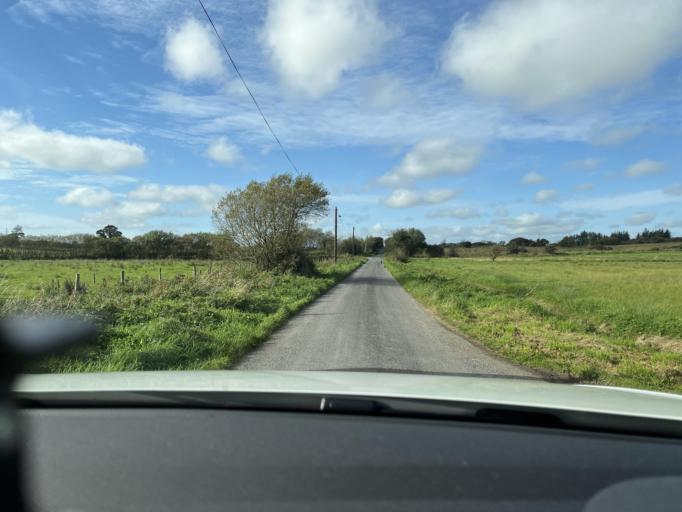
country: IE
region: Connaught
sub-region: Sligo
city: Ballymote
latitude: 54.0732
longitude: -8.4326
